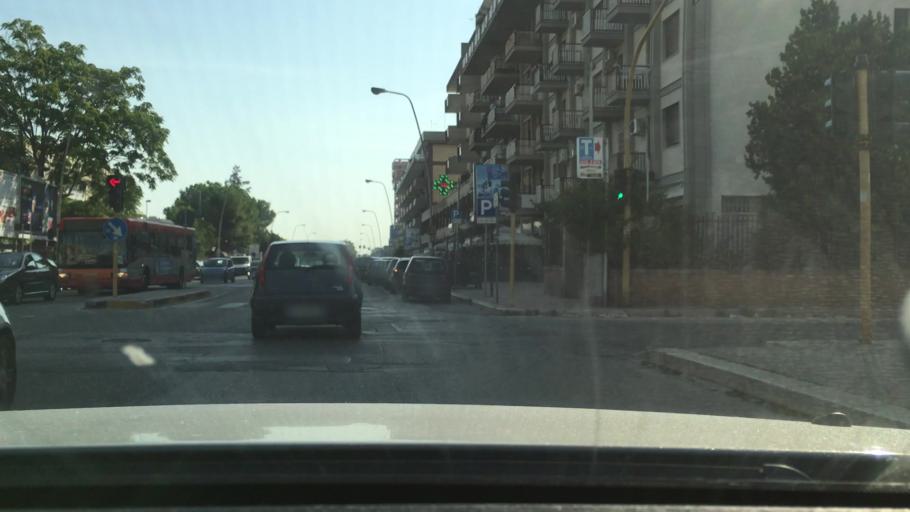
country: IT
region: Apulia
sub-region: Provincia di Bari
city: Bari
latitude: 41.1025
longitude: 16.8842
